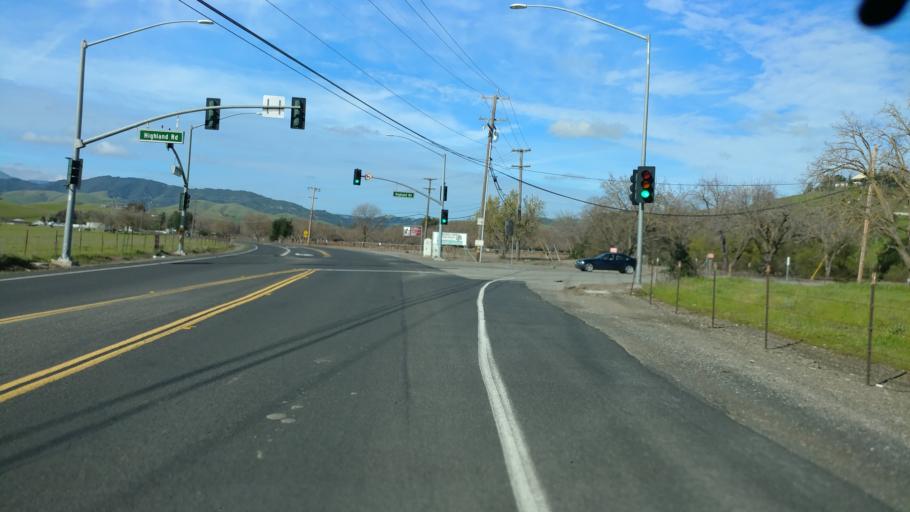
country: US
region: California
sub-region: Contra Costa County
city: Blackhawk
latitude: 37.7754
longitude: -121.8618
